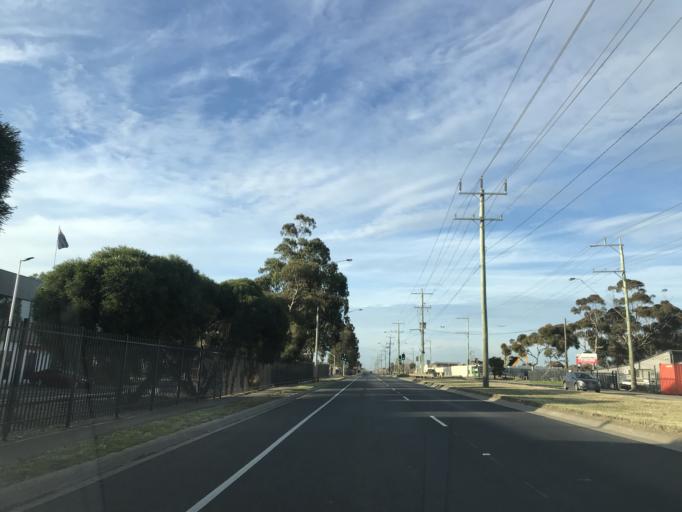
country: AU
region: Victoria
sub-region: Hobsons Bay
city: Laverton
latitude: -37.8368
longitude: 144.7835
